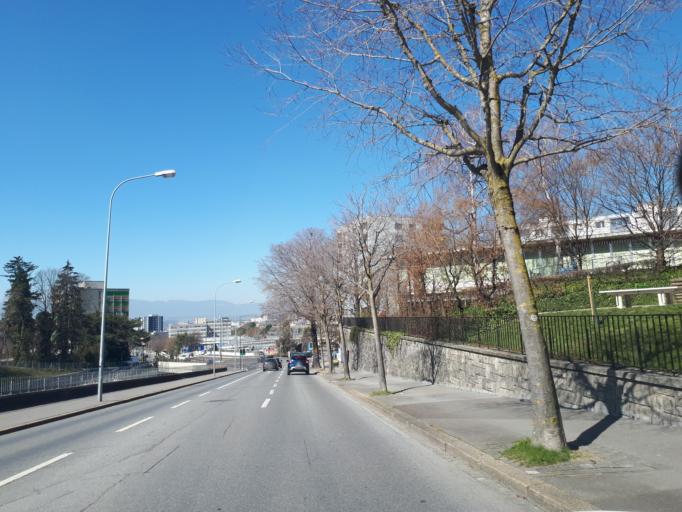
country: CH
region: Vaud
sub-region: Lausanne District
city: Lausanne
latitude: 46.5202
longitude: 6.6175
